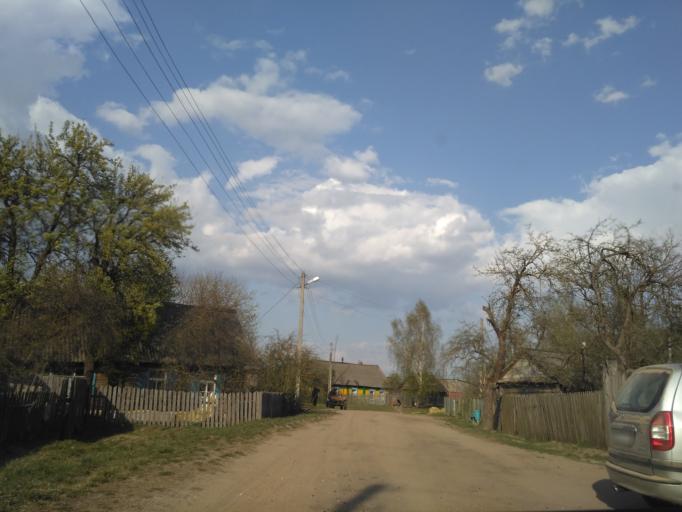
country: BY
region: Minsk
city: Khalopyenichy
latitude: 54.5075
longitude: 28.8541
